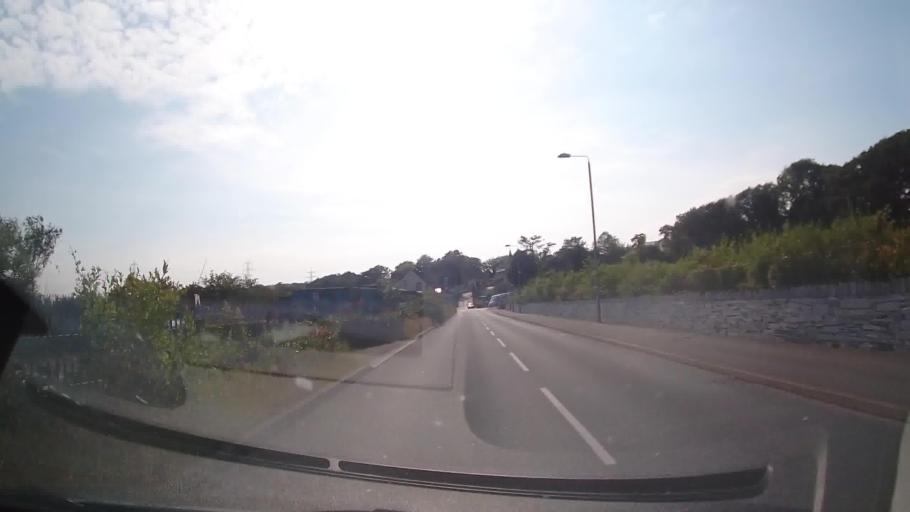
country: GB
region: Wales
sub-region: Gwynedd
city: Penrhyndeudraeth
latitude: 52.9291
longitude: -4.0633
